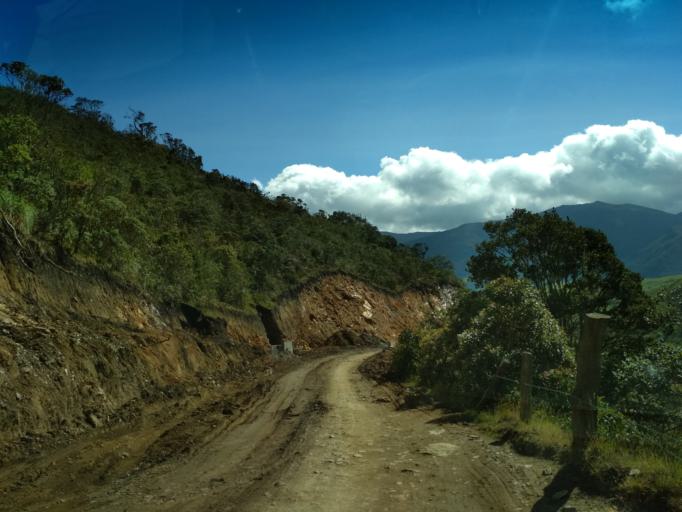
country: CO
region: Cauca
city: Silvia
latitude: 2.6944
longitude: -76.3310
